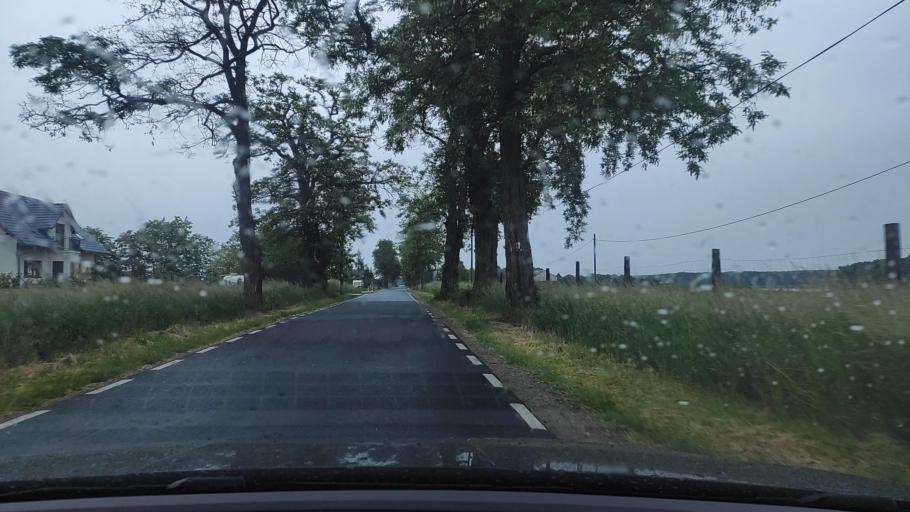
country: PL
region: Greater Poland Voivodeship
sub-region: Powiat poznanski
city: Kobylnica
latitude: 52.4826
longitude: 17.1608
